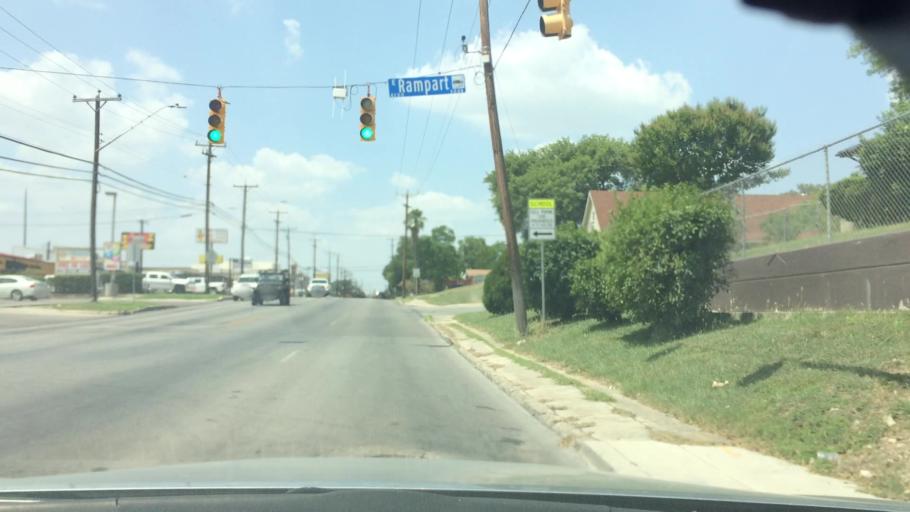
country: US
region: Texas
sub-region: Bexar County
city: Castle Hills
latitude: 29.5137
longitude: -98.4917
